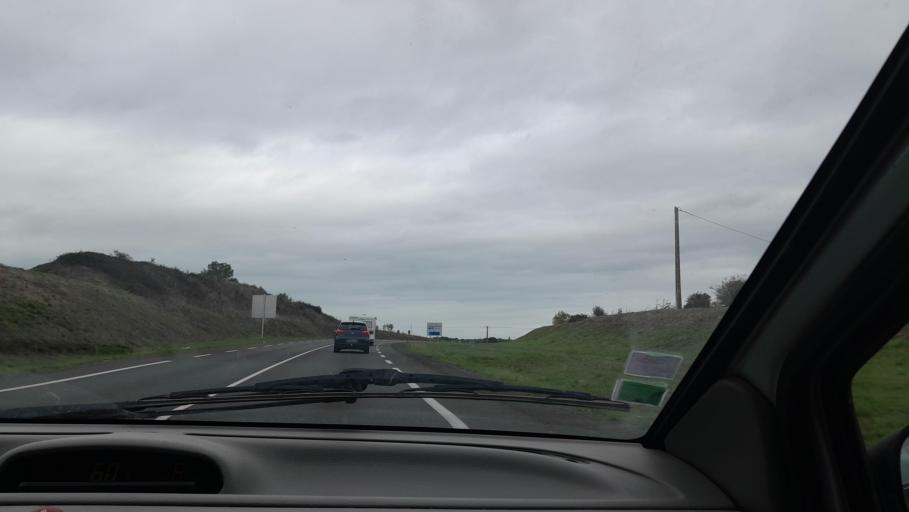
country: FR
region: Pays de la Loire
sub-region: Departement de la Loire-Atlantique
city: Saint-Gereon
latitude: 47.3885
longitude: -1.2000
